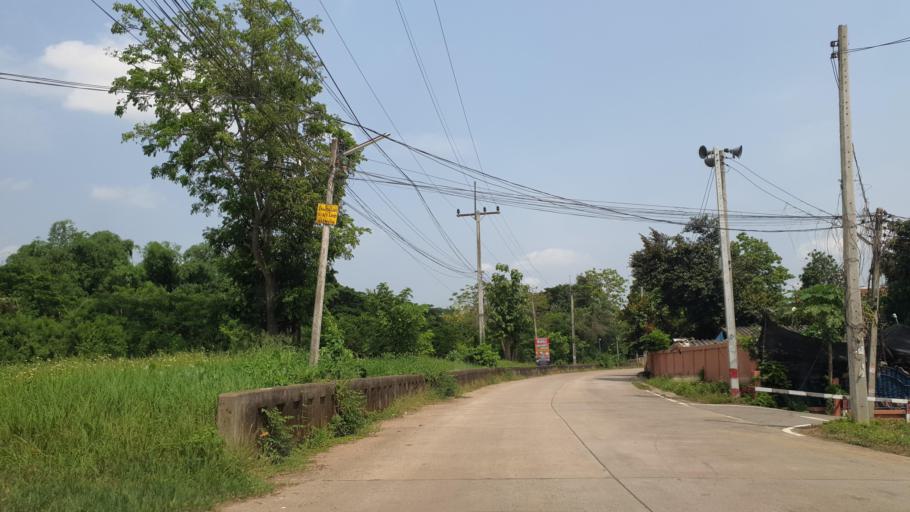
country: TH
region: Lamphun
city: Lamphun
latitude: 18.6016
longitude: 99.0295
